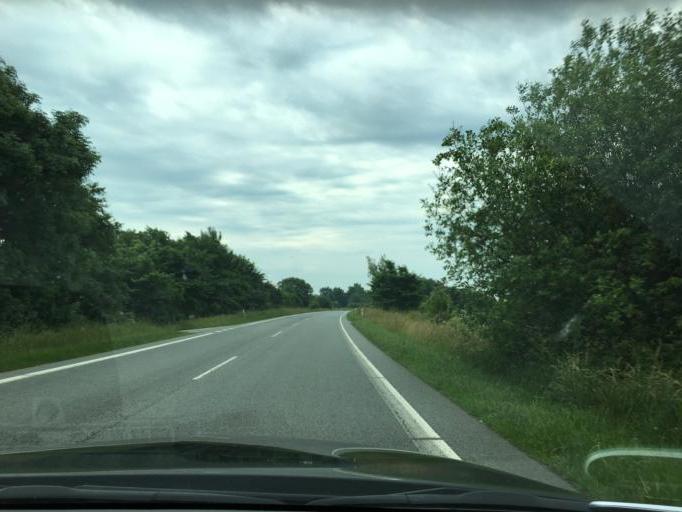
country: DK
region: South Denmark
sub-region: Vejle Kommune
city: Vejle
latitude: 55.6136
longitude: 9.4973
